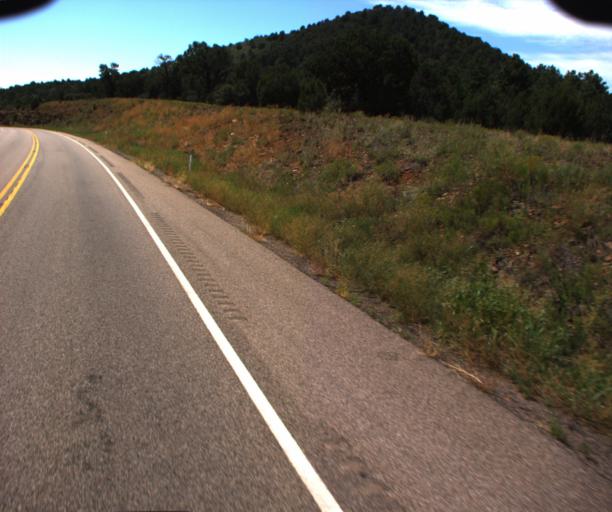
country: US
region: Arizona
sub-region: Gila County
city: San Carlos
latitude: 33.6594
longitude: -110.5718
